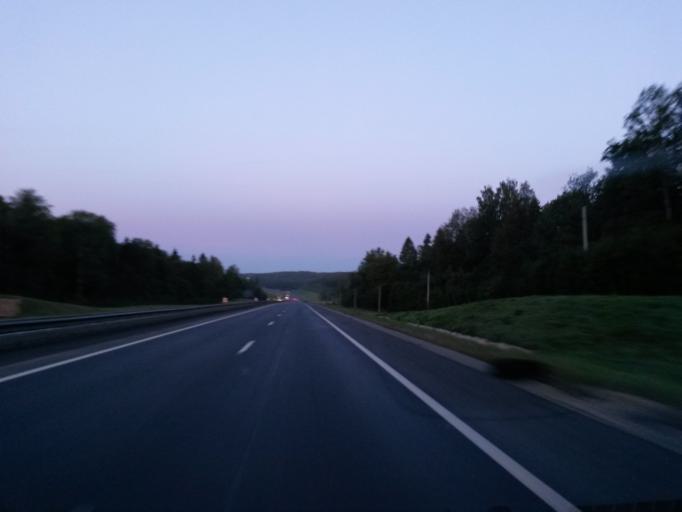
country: RU
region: Vladimir
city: Arsaki
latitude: 56.4882
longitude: 38.4286
